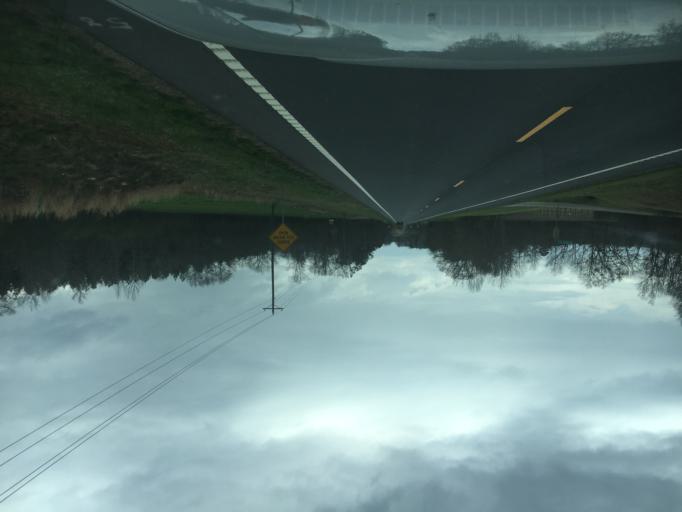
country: US
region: South Carolina
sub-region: Oconee County
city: Walhalla
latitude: 34.7894
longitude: -83.0220
